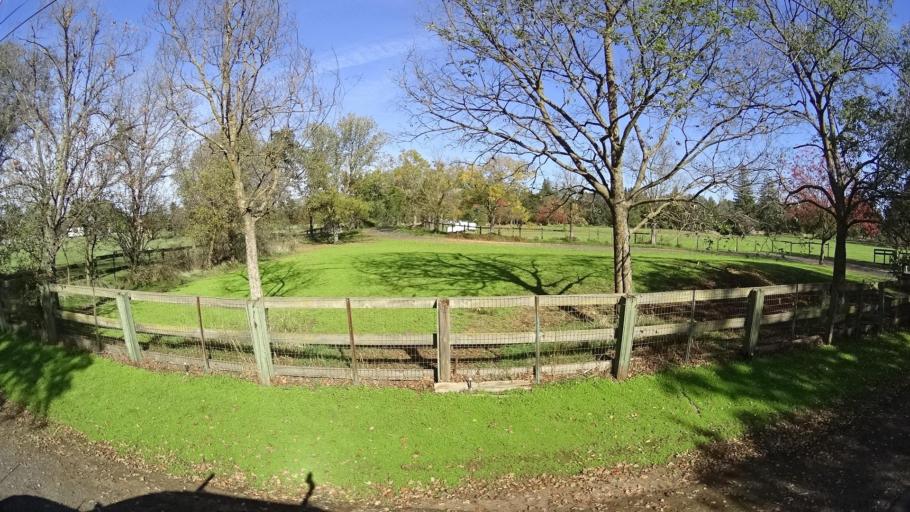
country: US
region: California
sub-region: Sacramento County
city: Wilton
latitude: 38.4336
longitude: -121.2941
